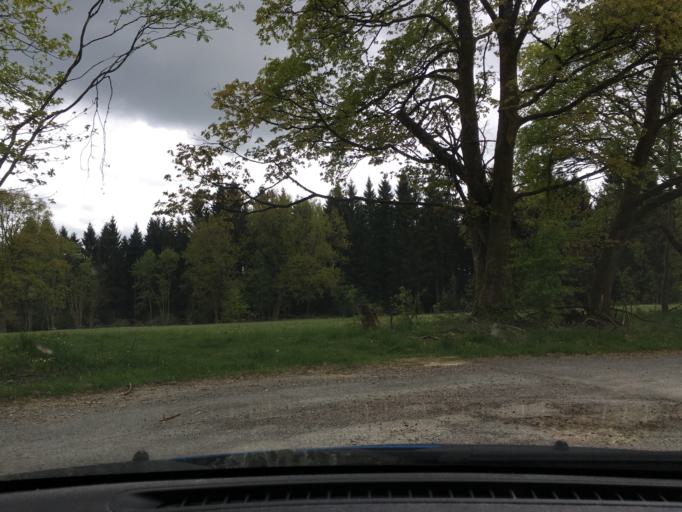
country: DE
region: Lower Saxony
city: Bevern
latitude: 51.7671
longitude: 9.5302
